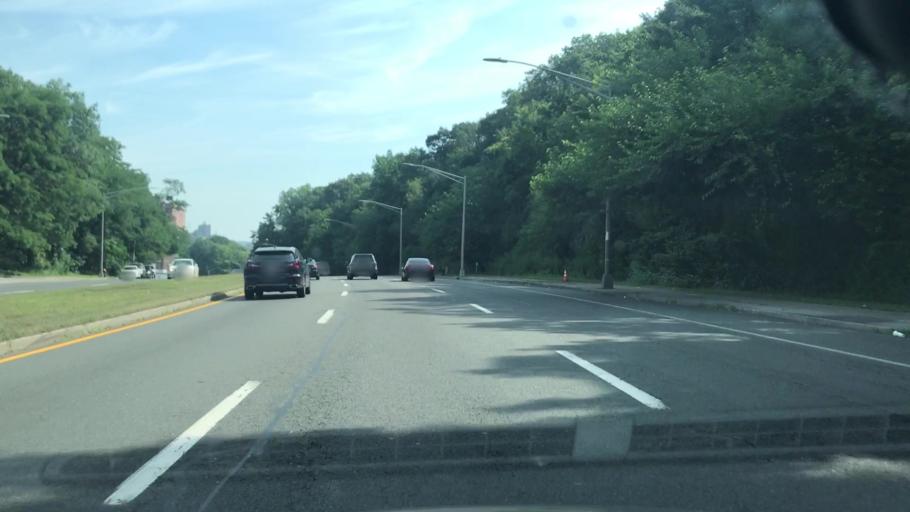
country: US
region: New York
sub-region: Westchester County
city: Bronxville
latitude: 40.9409
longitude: -73.8531
